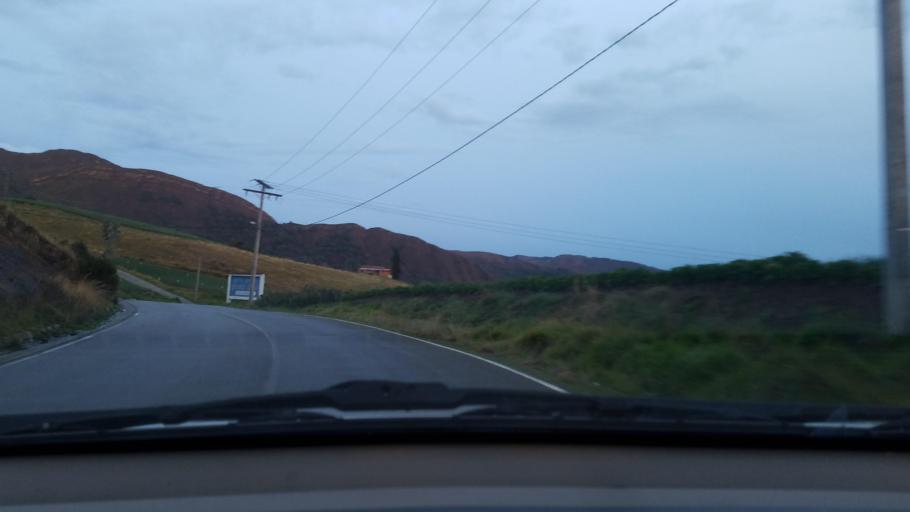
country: CO
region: Boyaca
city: Aquitania
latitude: 5.5710
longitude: -72.8936
